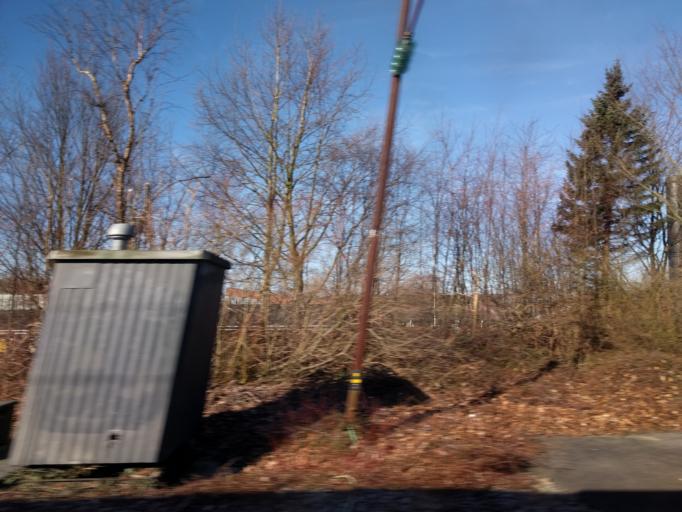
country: DK
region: Capital Region
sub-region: Rudersdal Kommune
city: Trorod
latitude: 55.8521
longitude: 12.5611
